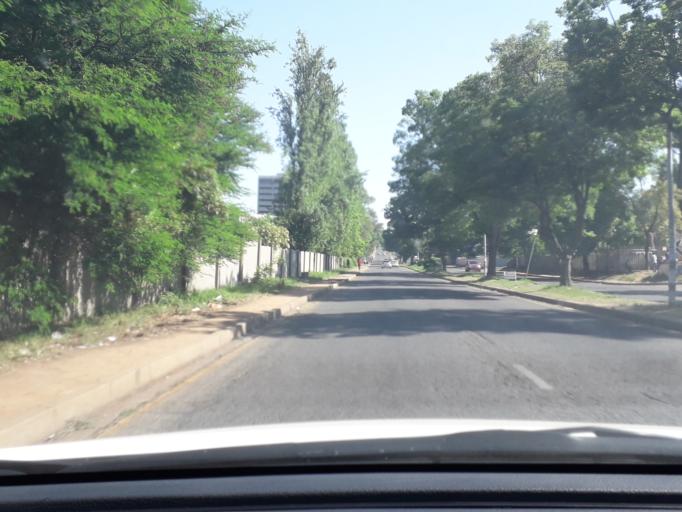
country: ZA
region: Gauteng
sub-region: City of Johannesburg Metropolitan Municipality
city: Johannesburg
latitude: -26.1244
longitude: 27.9740
